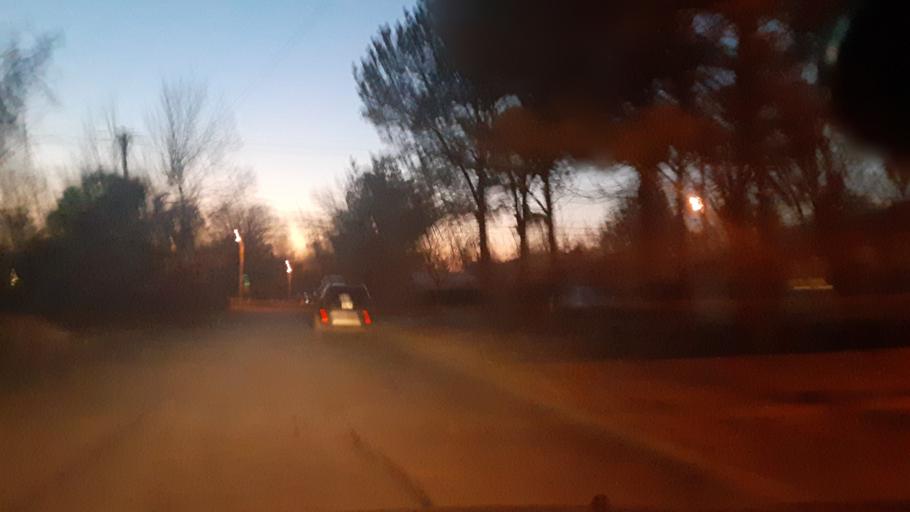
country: US
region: Oklahoma
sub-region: Payne County
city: Stillwater
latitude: 36.1113
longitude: -97.0806
